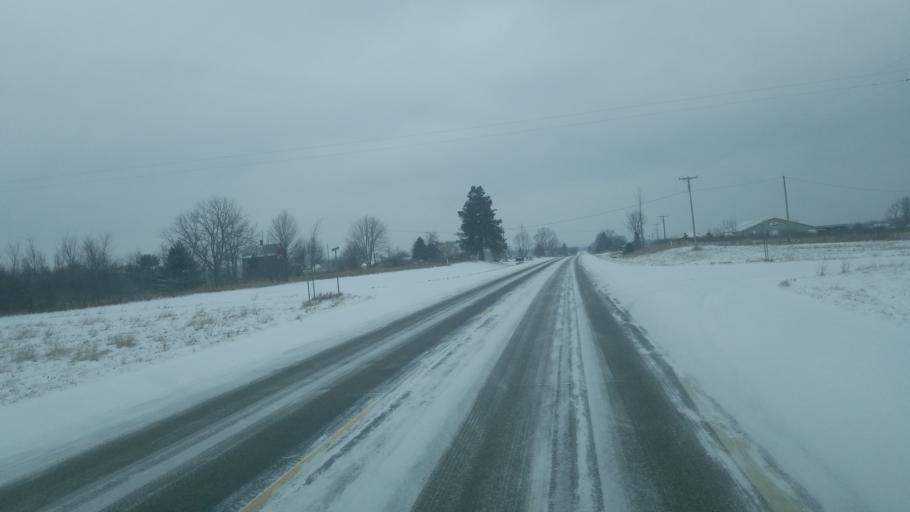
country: US
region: Michigan
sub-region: Osceola County
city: Evart
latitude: 43.9147
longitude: -85.1483
